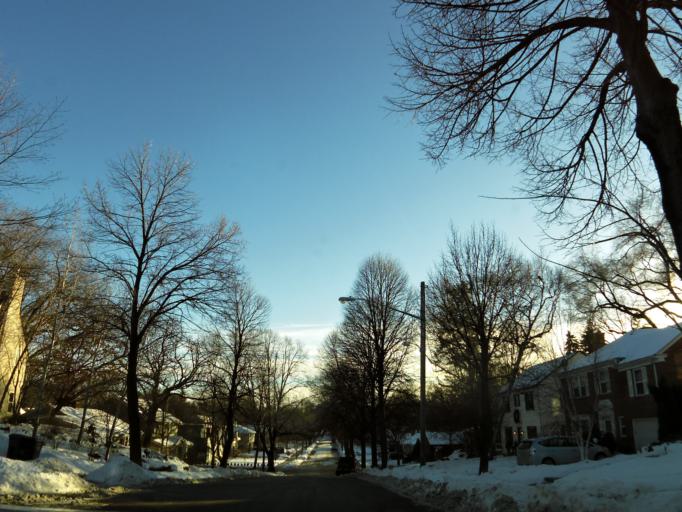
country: US
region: Minnesota
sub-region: Hennepin County
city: Saint Louis Park
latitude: 44.9331
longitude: -93.3227
